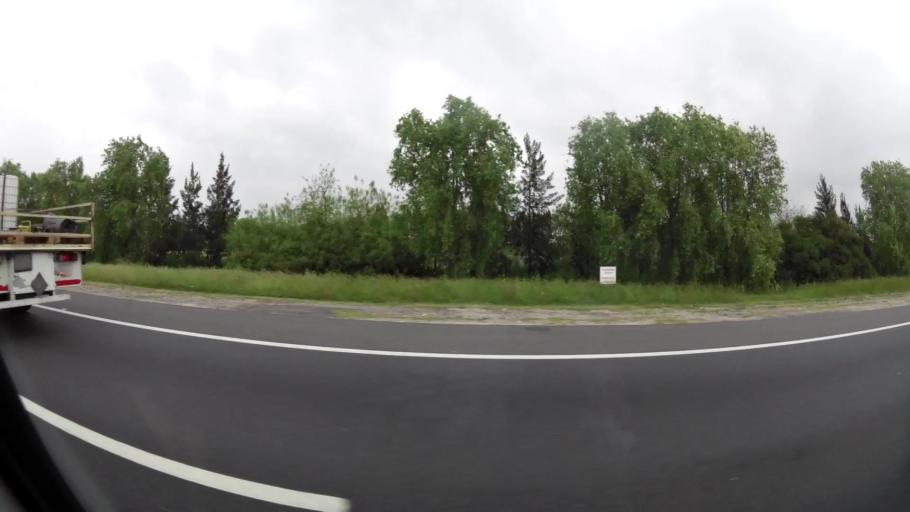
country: AR
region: Buenos Aires
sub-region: Partido de Quilmes
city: Quilmes
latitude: -34.6950
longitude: -58.2802
